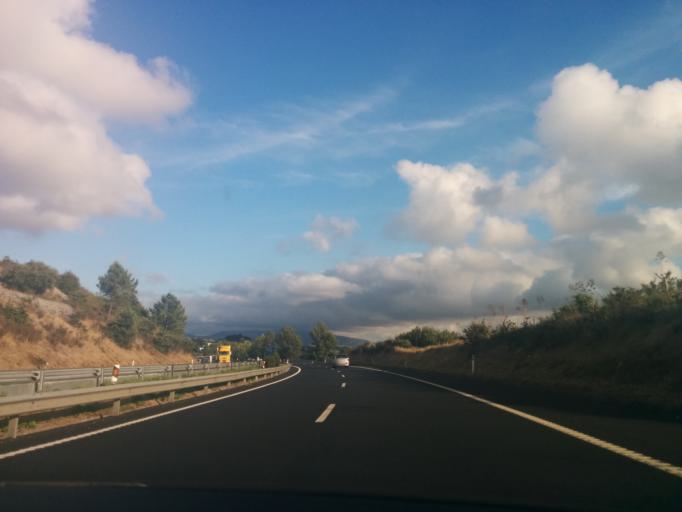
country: PT
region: Leiria
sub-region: Bombarral
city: Bombarral
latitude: 39.3044
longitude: -9.1684
